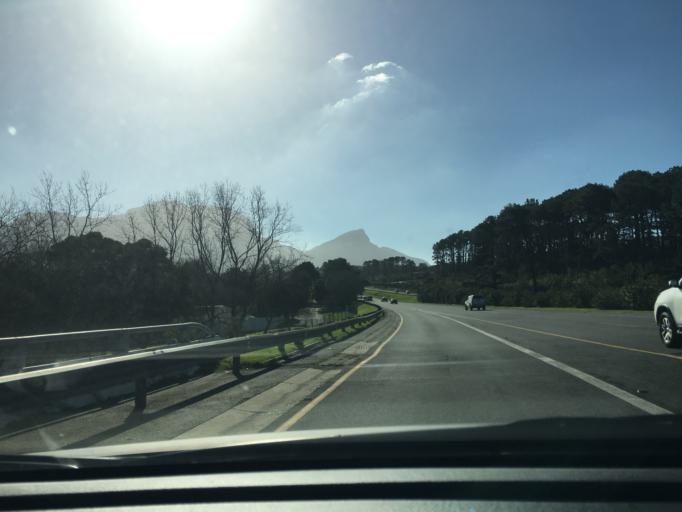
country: ZA
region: Western Cape
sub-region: City of Cape Town
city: Bergvliet
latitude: -34.0138
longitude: 18.4536
